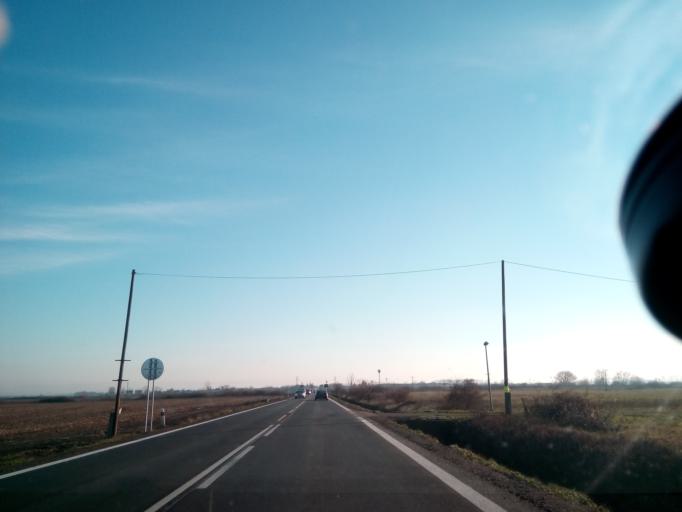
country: SK
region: Kosicky
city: Secovce
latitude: 48.7020
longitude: 21.6889
